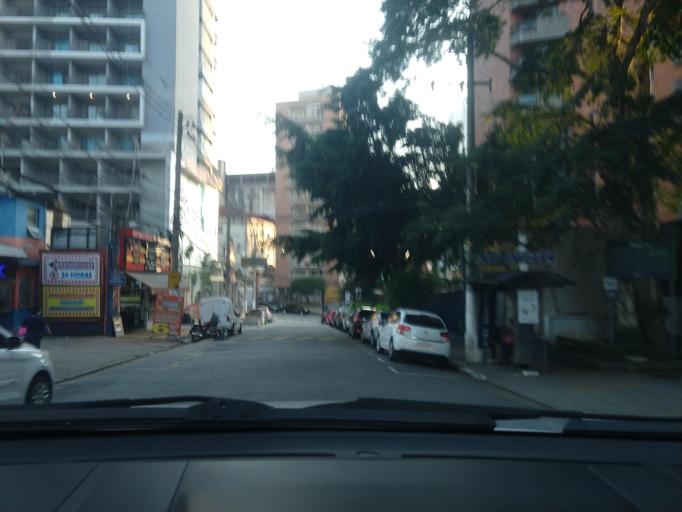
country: BR
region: Sao Paulo
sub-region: Sao Paulo
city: Sao Paulo
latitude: -23.5813
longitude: -46.6405
